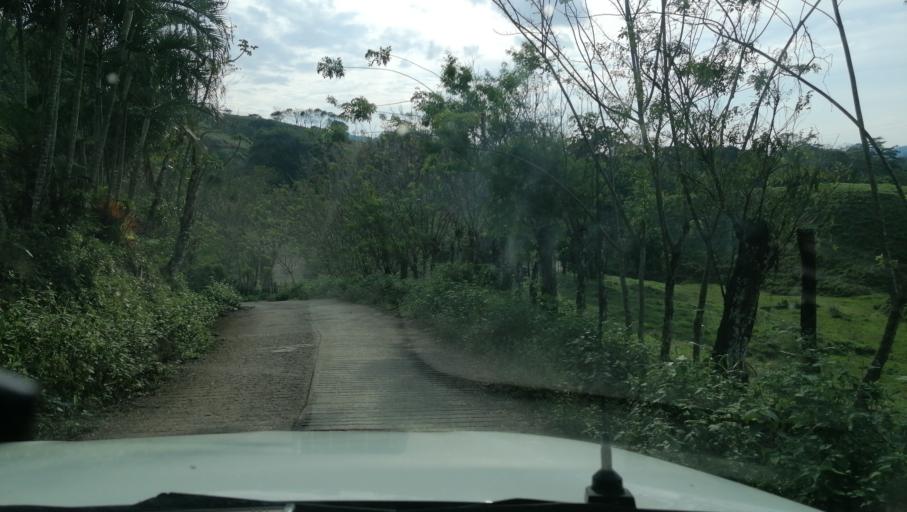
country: MX
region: Chiapas
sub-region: Juarez
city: El Triunfo 1ra. Seccion (Cardona)
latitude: 17.4849
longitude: -93.2401
